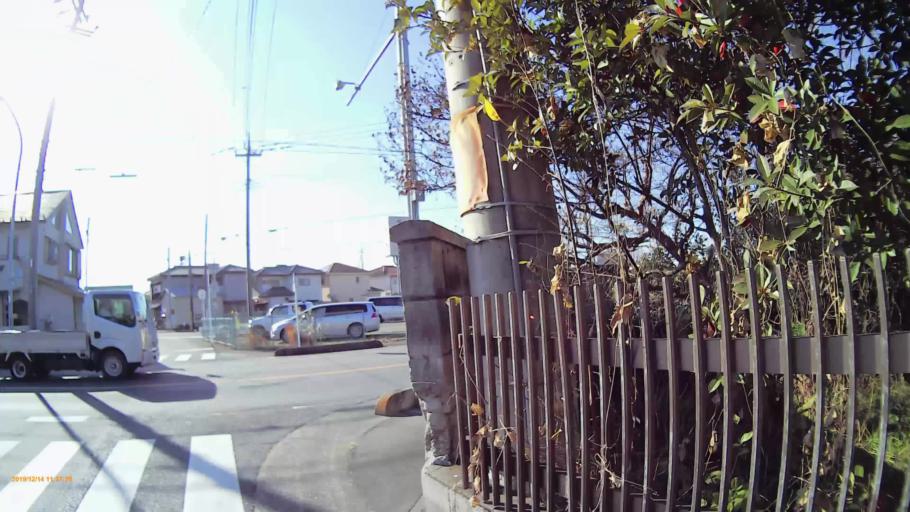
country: JP
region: Saitama
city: Kumagaya
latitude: 36.1315
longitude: 139.4001
